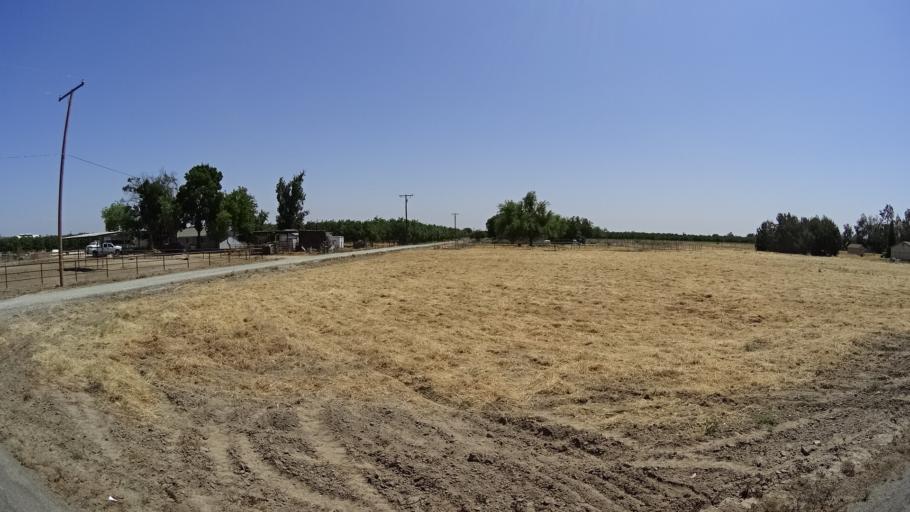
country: US
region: California
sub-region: Kings County
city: Armona
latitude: 36.2872
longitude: -119.6911
